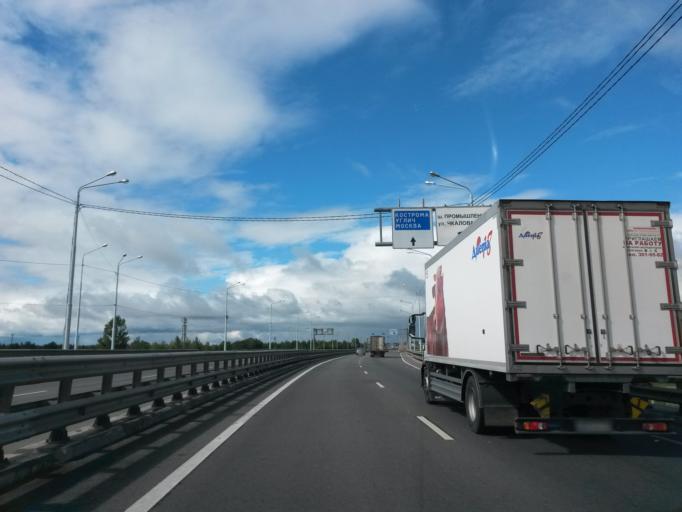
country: RU
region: Jaroslavl
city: Yaroslavl
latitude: 57.6674
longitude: 39.8199
